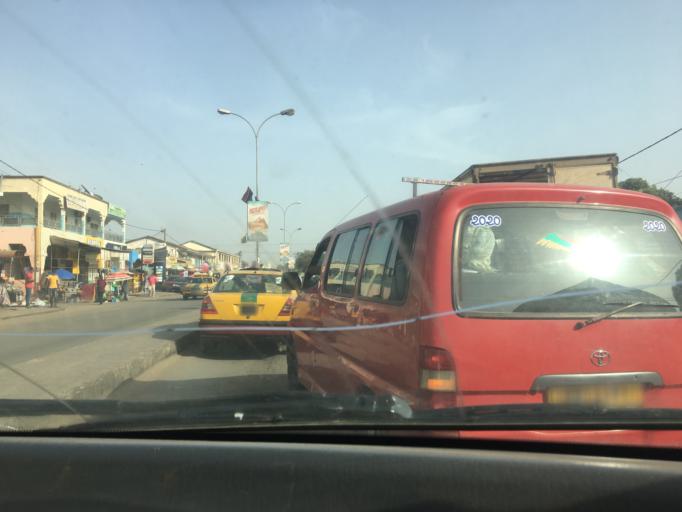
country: GM
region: Western
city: Abuko
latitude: 13.4142
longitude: -16.6718
